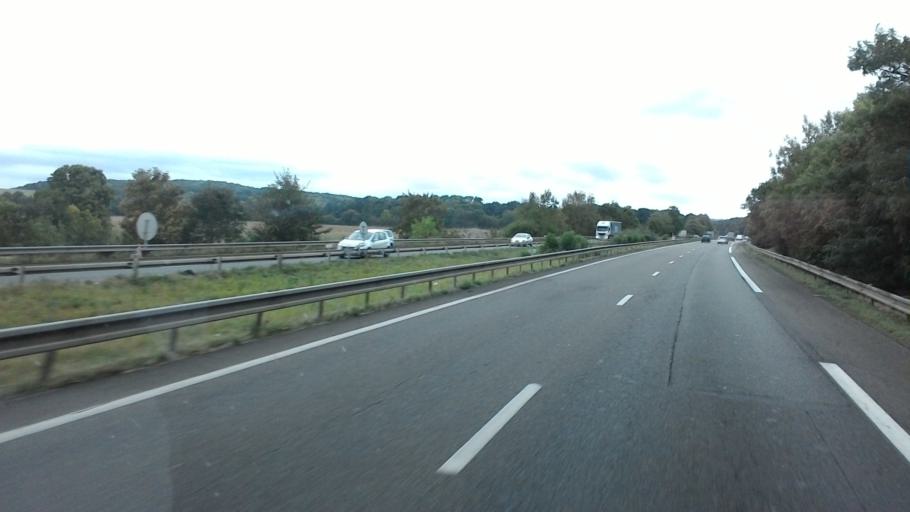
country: FR
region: Lorraine
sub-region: Departement de la Moselle
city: Augny
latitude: 49.0447
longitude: 6.1120
